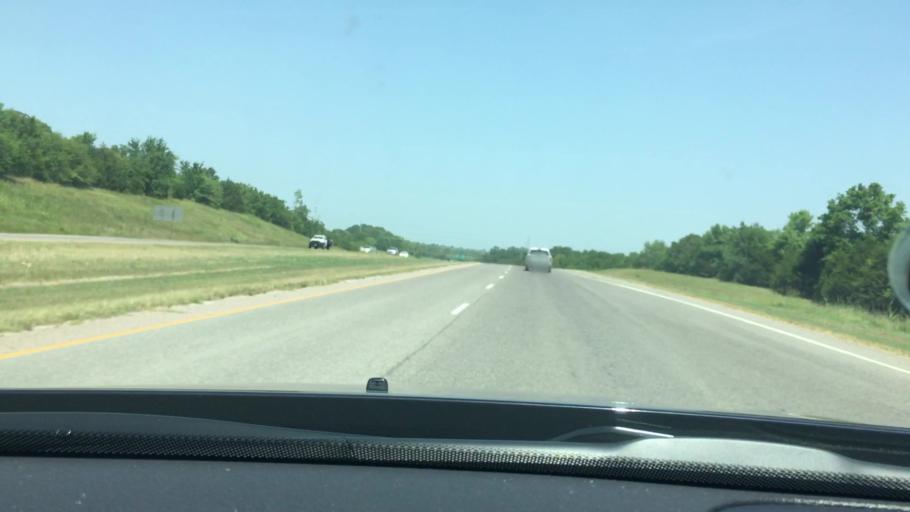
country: US
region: Oklahoma
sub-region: Pontotoc County
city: Ada
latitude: 34.7410
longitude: -96.6468
